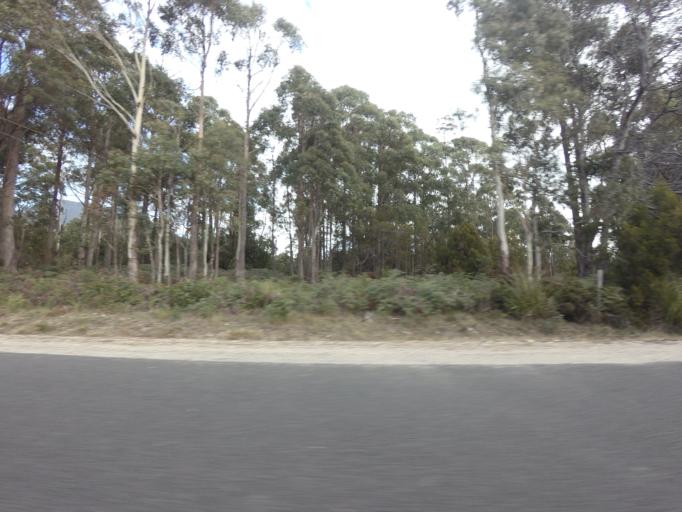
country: AU
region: Tasmania
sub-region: Meander Valley
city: Deloraine
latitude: -41.6179
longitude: 146.6936
